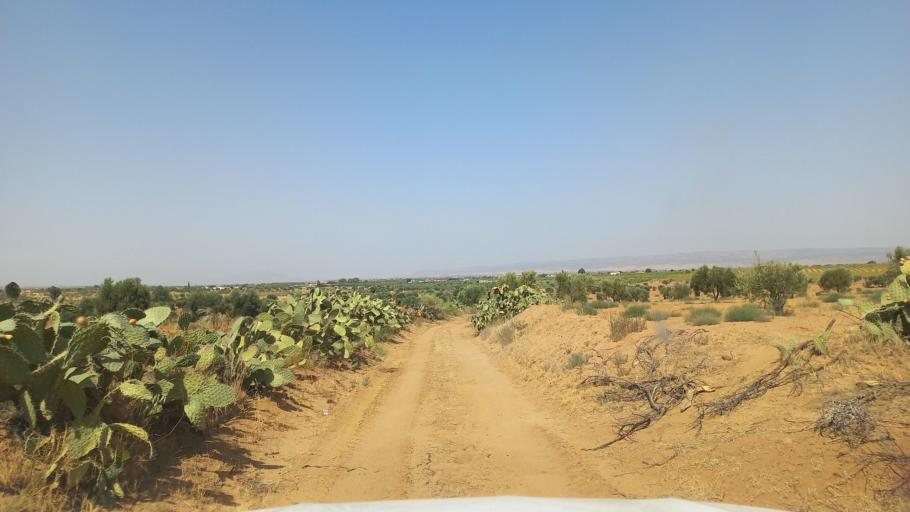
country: TN
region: Al Qasrayn
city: Kasserine
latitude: 35.2401
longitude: 9.0647
